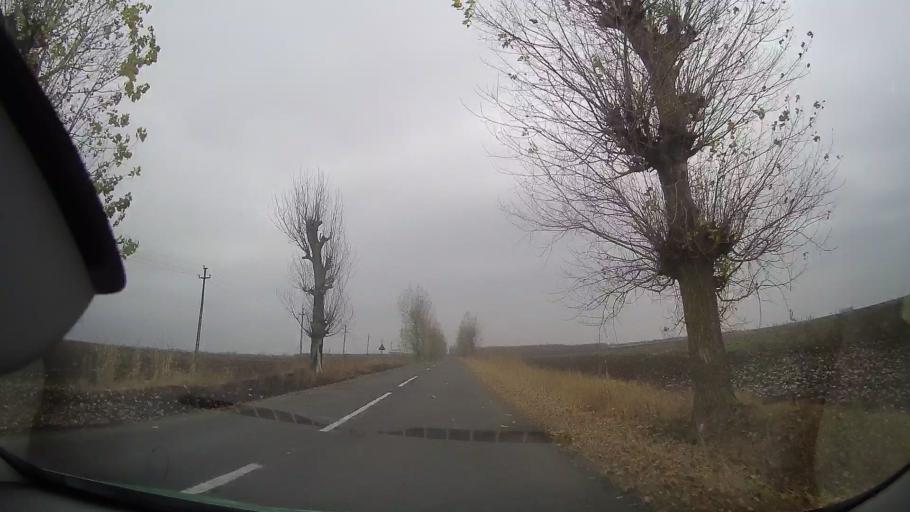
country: RO
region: Ialomita
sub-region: Comuna Grindu
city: Grindu
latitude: 44.7910
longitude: 26.9005
